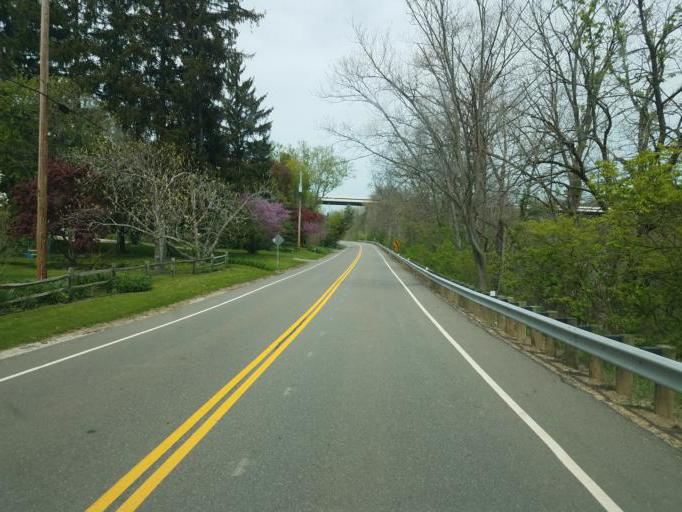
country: US
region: Ohio
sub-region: Summit County
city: Peninsula
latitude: 41.2573
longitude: -81.5576
